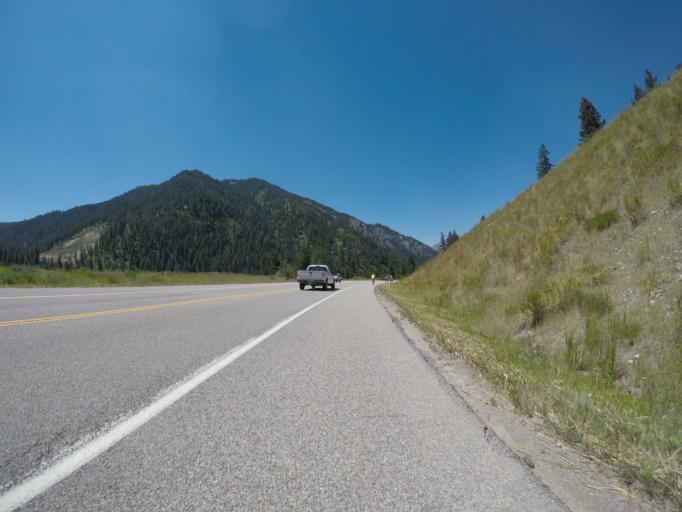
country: US
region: Wyoming
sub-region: Teton County
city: Hoback
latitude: 43.1961
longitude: -110.8733
